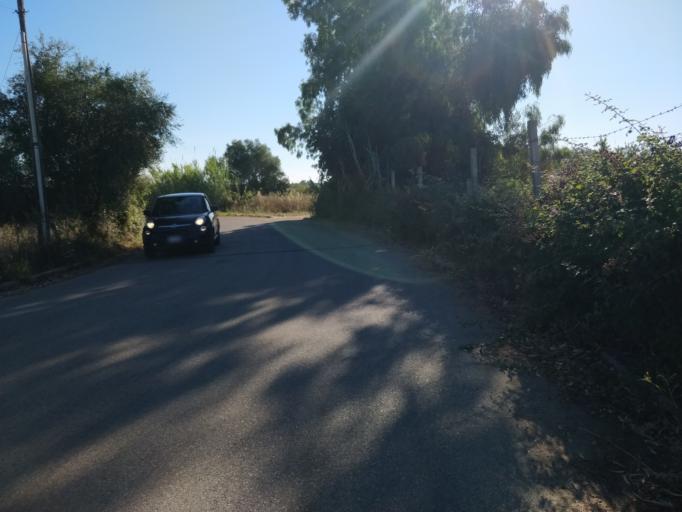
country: IT
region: Sardinia
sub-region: Provincia di Ogliastra
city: Girasole
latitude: 39.9527
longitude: 9.6712
